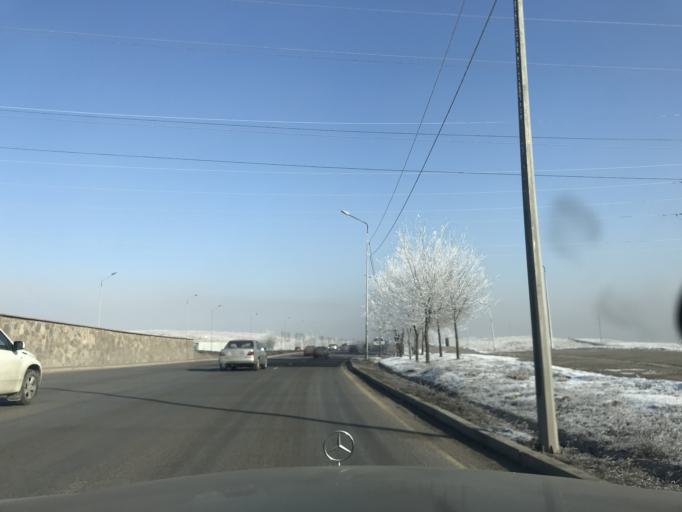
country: KZ
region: Almaty Oblysy
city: Burunday
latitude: 43.2885
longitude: 76.8271
